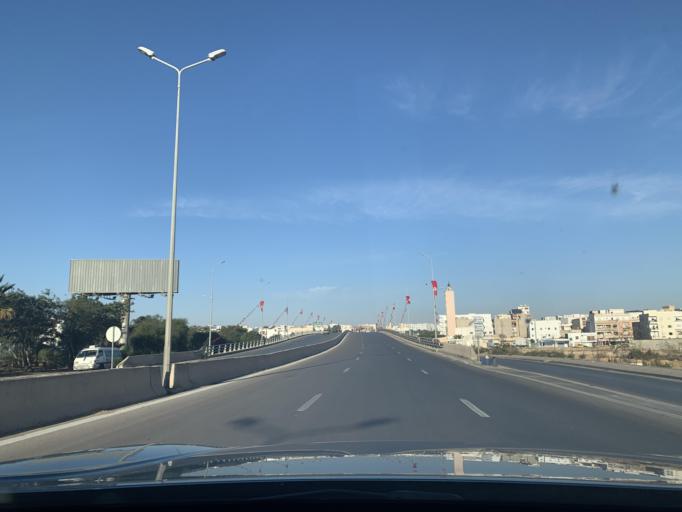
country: DZ
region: Souk Ahras
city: Souk Ahras
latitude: 36.3659
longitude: 8.0022
